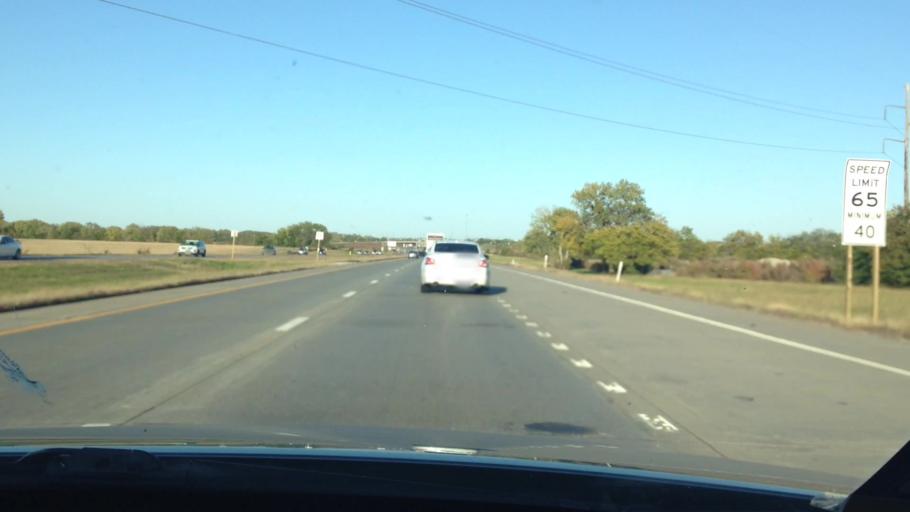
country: US
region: Kansas
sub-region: Johnson County
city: Olathe
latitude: 38.8327
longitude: -94.8493
